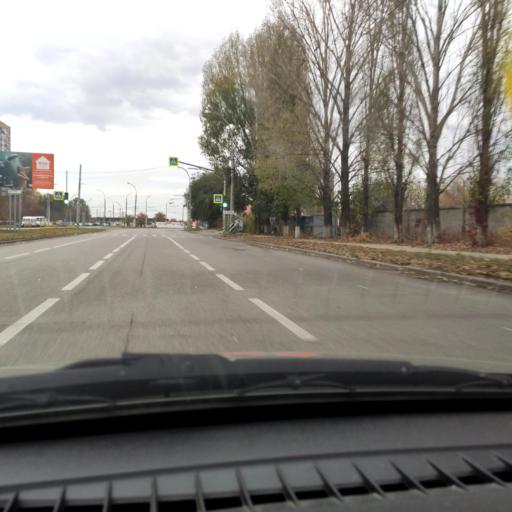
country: RU
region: Samara
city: Tol'yatti
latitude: 53.5122
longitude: 49.2569
